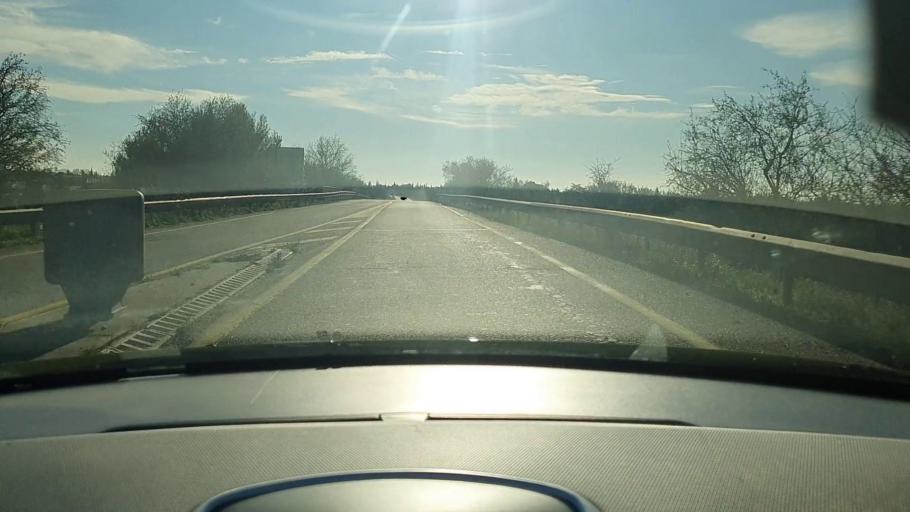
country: FR
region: Languedoc-Roussillon
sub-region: Departement du Gard
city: Beaucaire
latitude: 43.8057
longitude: 4.6092
